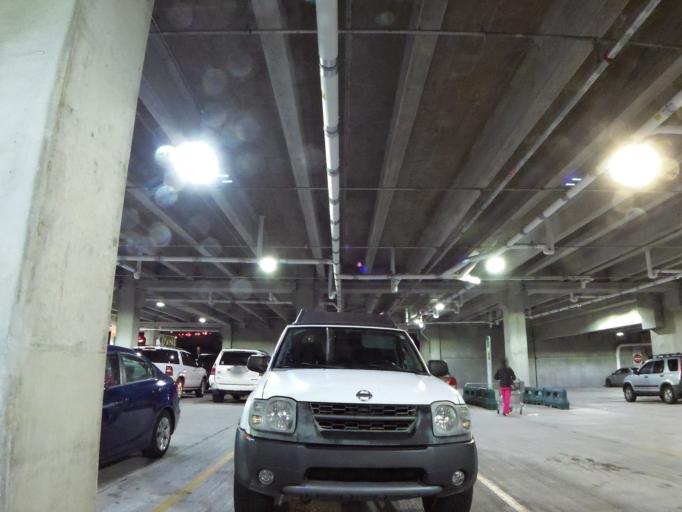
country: US
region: Tennessee
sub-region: Knox County
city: Knoxville
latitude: 35.9496
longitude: -83.9415
